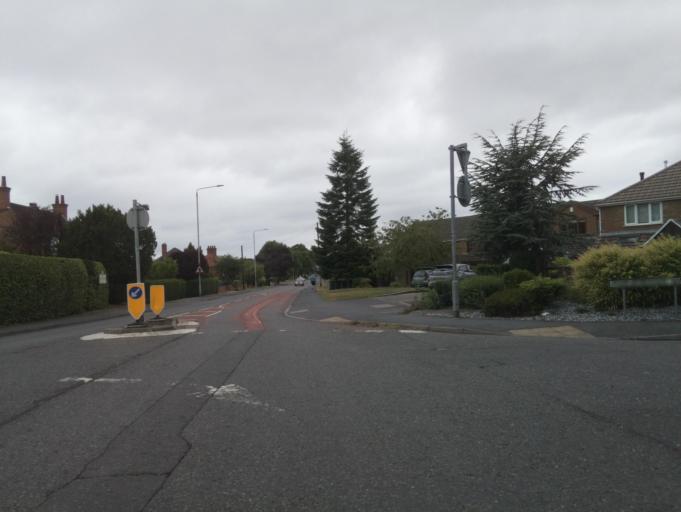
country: GB
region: England
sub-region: Leicestershire
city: Ashby de la Zouch
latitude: 52.7489
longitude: -1.4814
